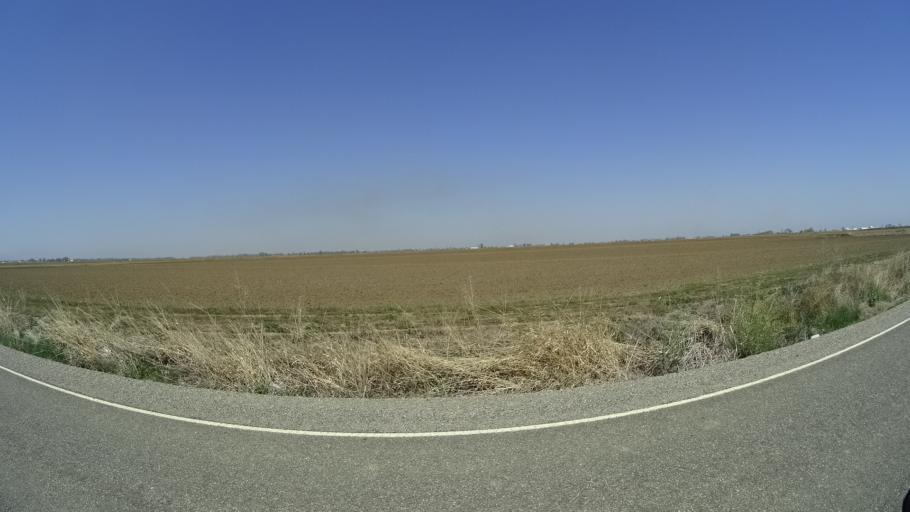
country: US
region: California
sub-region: Glenn County
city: Willows
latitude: 39.4947
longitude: -122.1492
